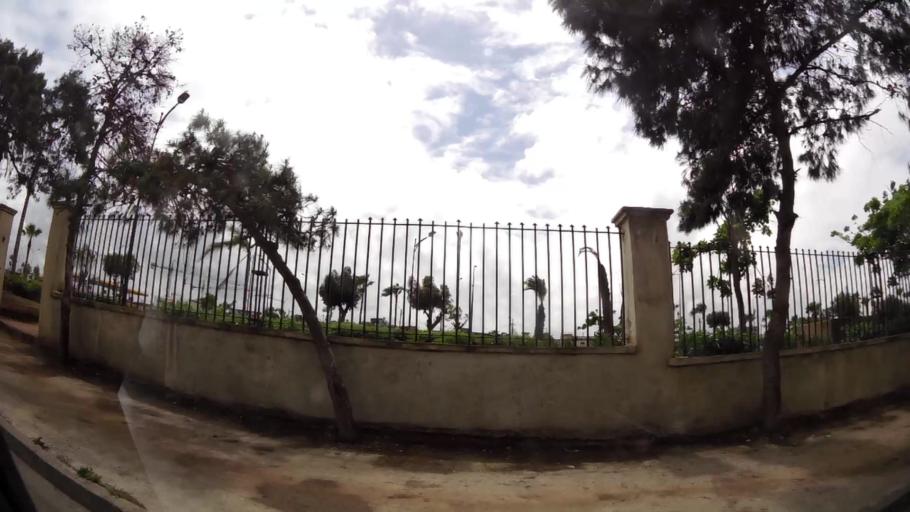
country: MA
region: Grand Casablanca
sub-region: Mediouna
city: Tit Mellil
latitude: 33.6019
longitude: -7.5154
